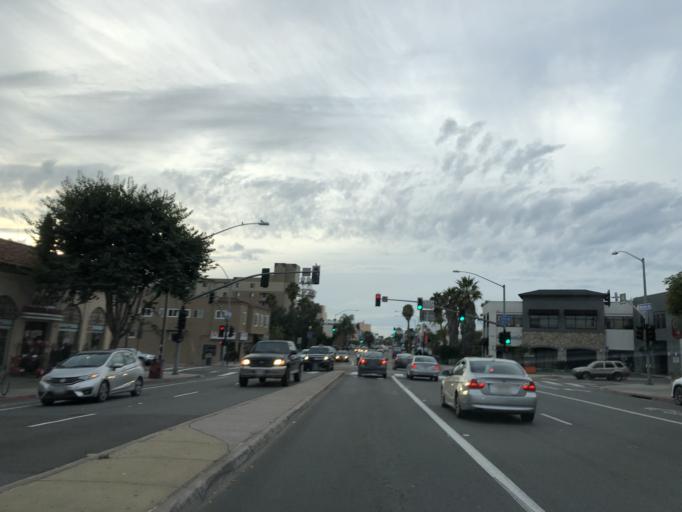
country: US
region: California
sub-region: San Diego County
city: San Diego
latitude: 32.7485
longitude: -117.1548
